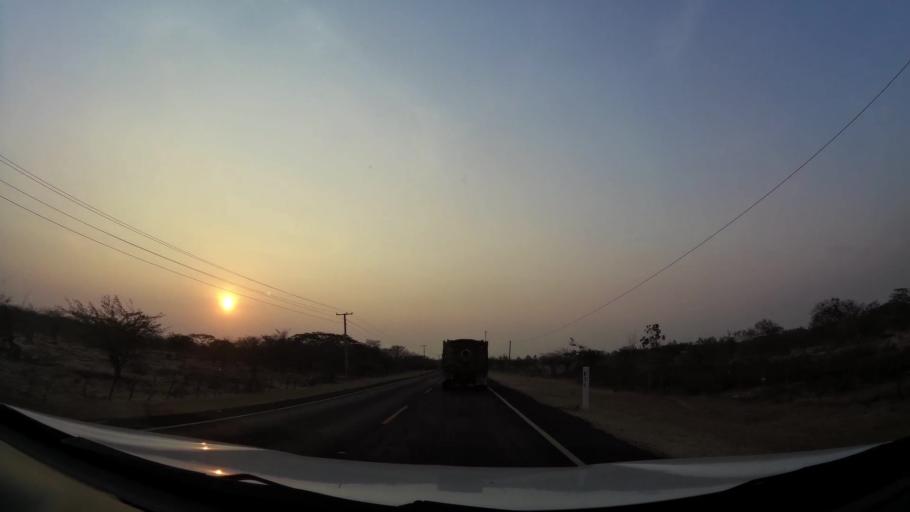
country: NI
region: Leon
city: La Paz Centro
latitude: 12.2931
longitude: -86.7643
